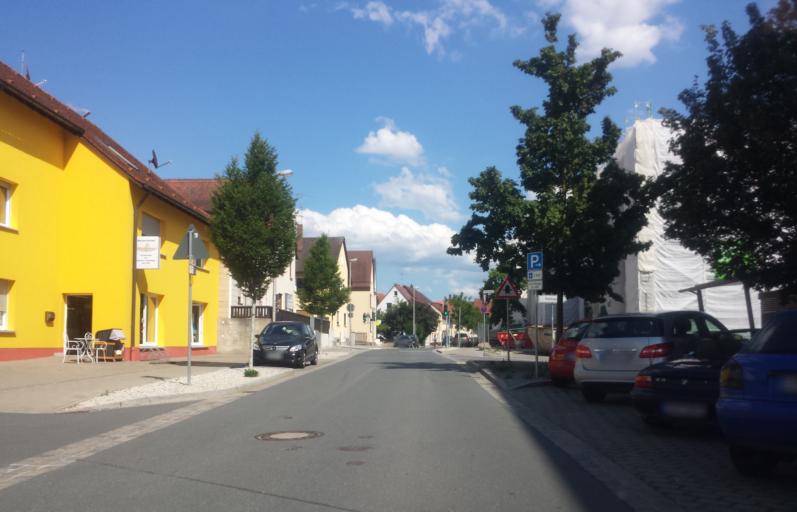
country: DE
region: Bavaria
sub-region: Regierungsbezirk Mittelfranken
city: Herzogenaurach
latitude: 49.5711
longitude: 10.8757
